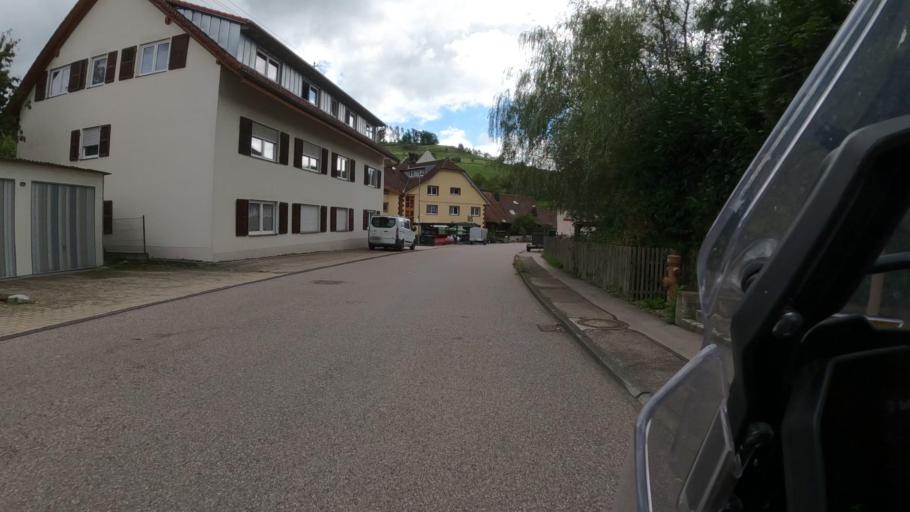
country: DE
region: Baden-Wuerttemberg
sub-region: Freiburg Region
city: Uhlingen-Birkendorf
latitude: 47.7031
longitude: 8.3447
